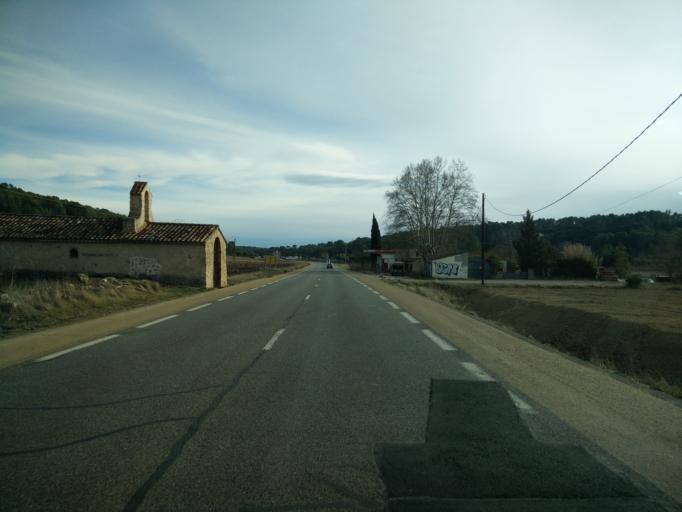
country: FR
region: Provence-Alpes-Cote d'Azur
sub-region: Departement du Var
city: Lorgues
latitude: 43.4774
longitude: 6.3735
